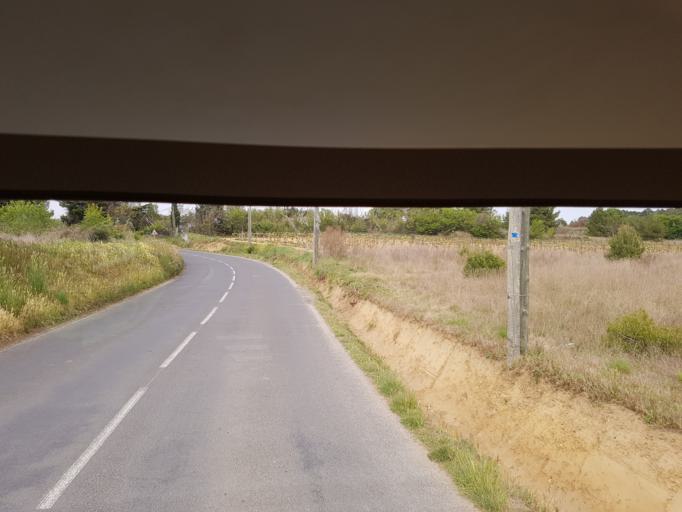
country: FR
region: Languedoc-Roussillon
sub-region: Departement de l'Aude
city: Fleury
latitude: 43.2219
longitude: 3.1318
